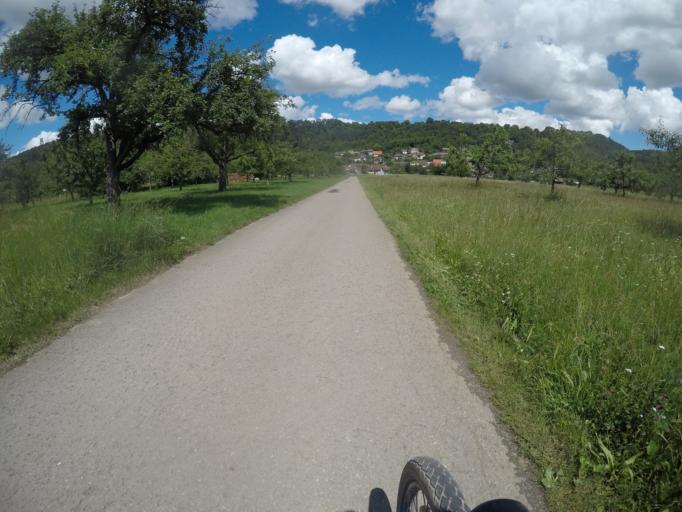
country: DE
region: Baden-Wuerttemberg
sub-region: Tuebingen Region
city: Haigerloch
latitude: 48.4448
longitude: 8.8062
